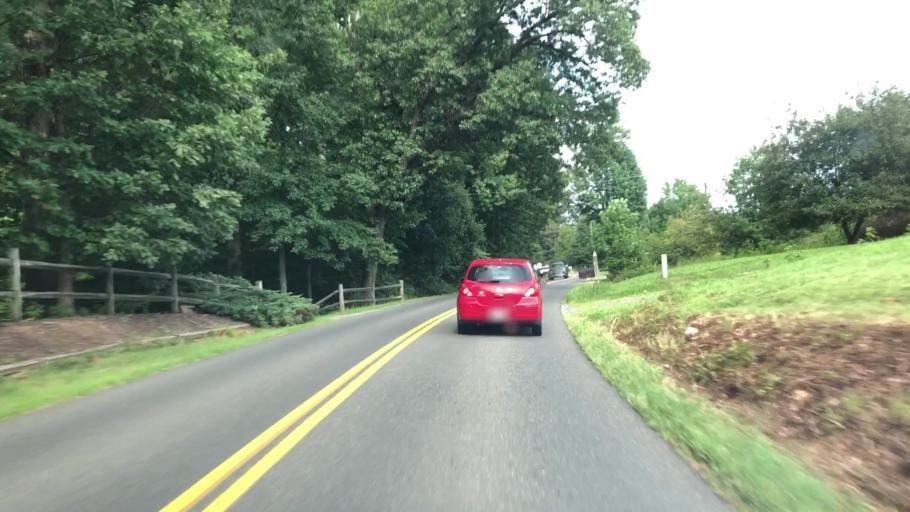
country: US
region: Virginia
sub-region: Stafford County
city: Falmouth
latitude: 38.3997
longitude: -77.5283
